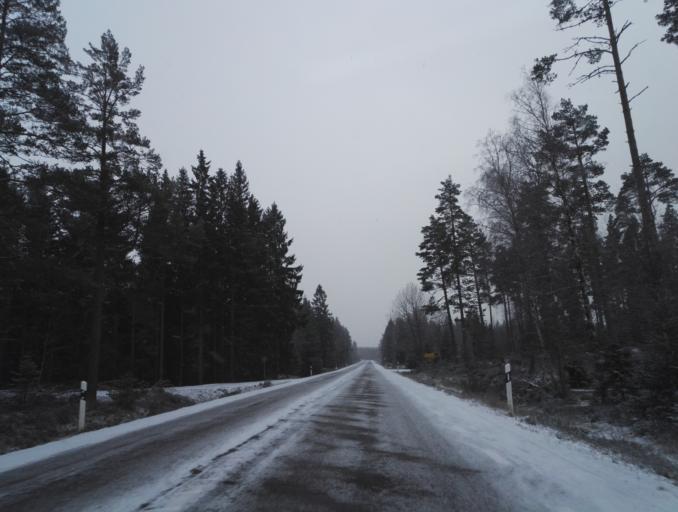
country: SE
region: Kronoberg
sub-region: Uppvidinge Kommun
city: Lenhovda
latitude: 56.8863
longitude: 15.3749
